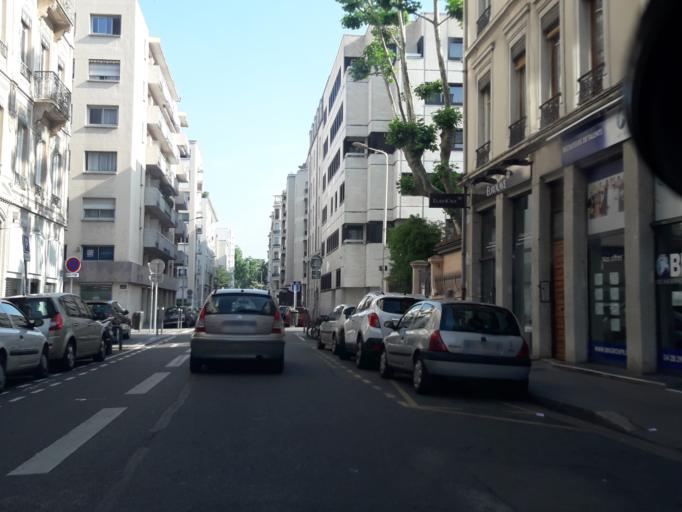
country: FR
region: Rhone-Alpes
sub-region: Departement du Rhone
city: Caluire-et-Cuire
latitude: 45.7706
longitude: 4.8522
